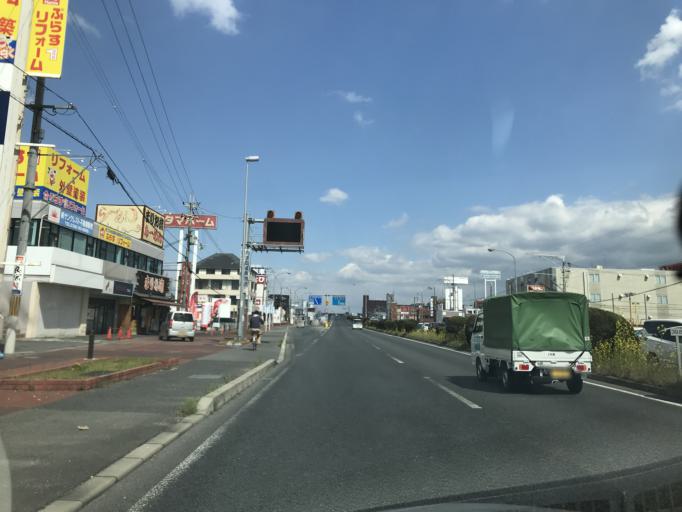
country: JP
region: Nara
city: Nara-shi
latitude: 34.6776
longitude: 135.8003
